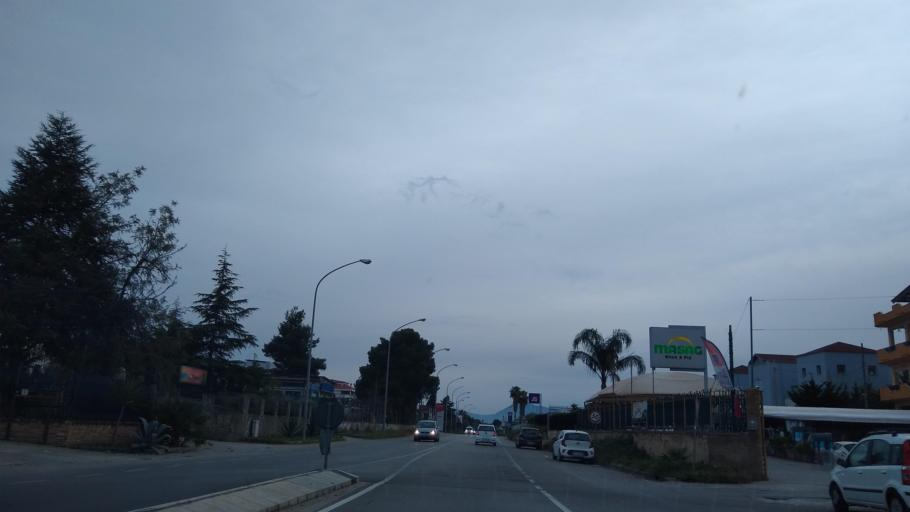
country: IT
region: Sicily
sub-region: Palermo
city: Partinico
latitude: 38.0392
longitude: 13.1068
